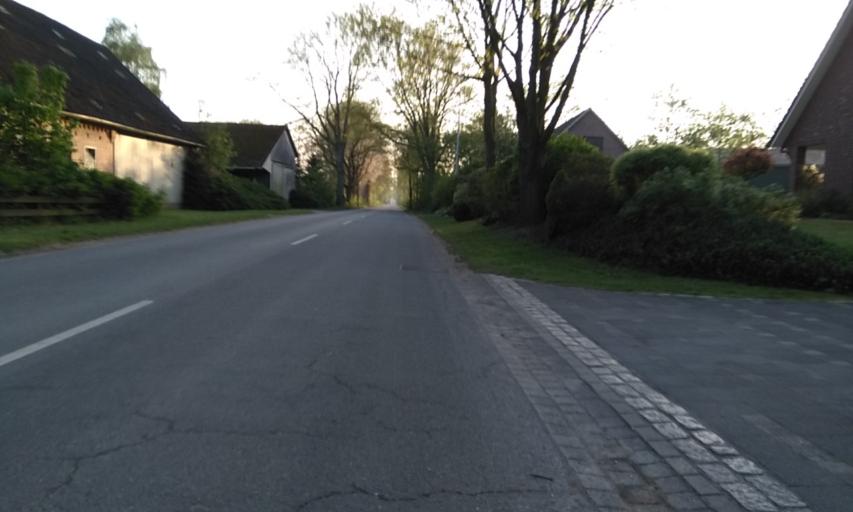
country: DE
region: Lower Saxony
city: Deinste
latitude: 53.5108
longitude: 9.4788
